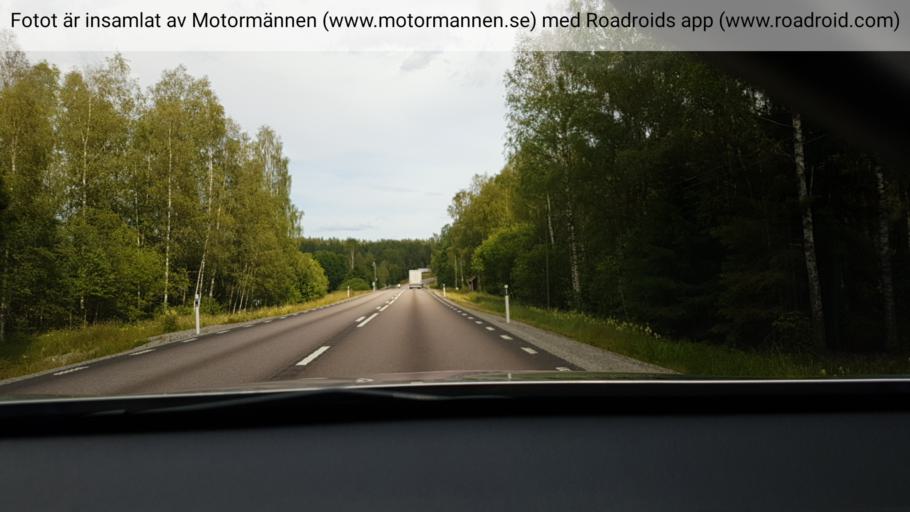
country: SE
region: Vaermland
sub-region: Sunne Kommun
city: Sunne
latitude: 59.6652
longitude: 12.8985
